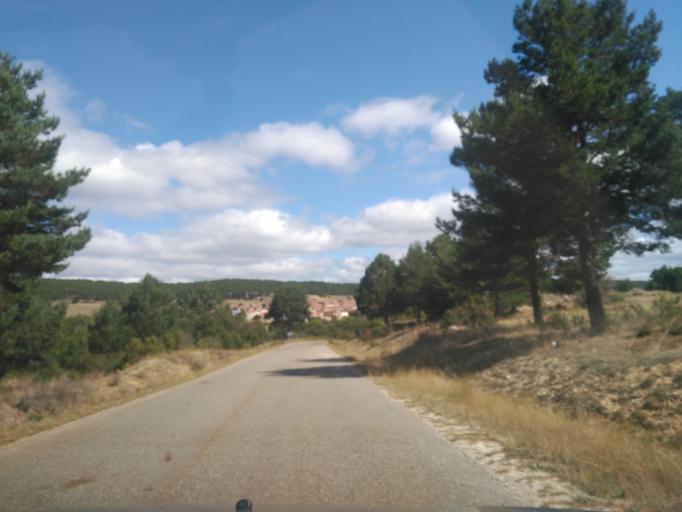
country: ES
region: Castille and Leon
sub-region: Provincia de Soria
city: Espejon
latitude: 41.8485
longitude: -3.2301
